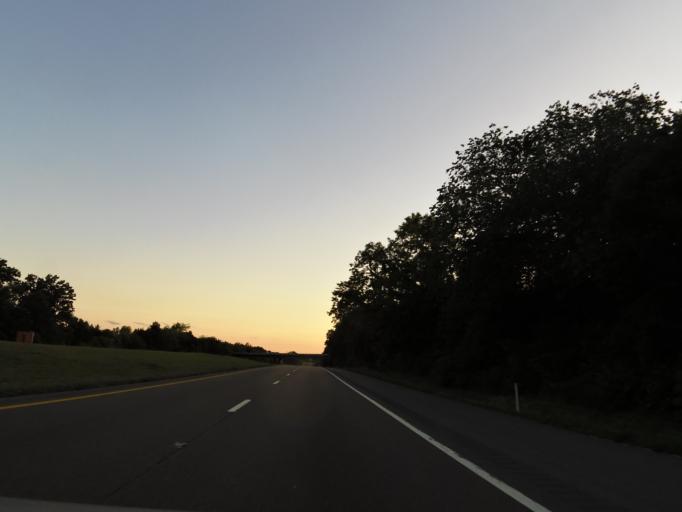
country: US
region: Tennessee
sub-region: Hamblen County
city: Morristown
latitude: 36.1746
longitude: -83.2084
